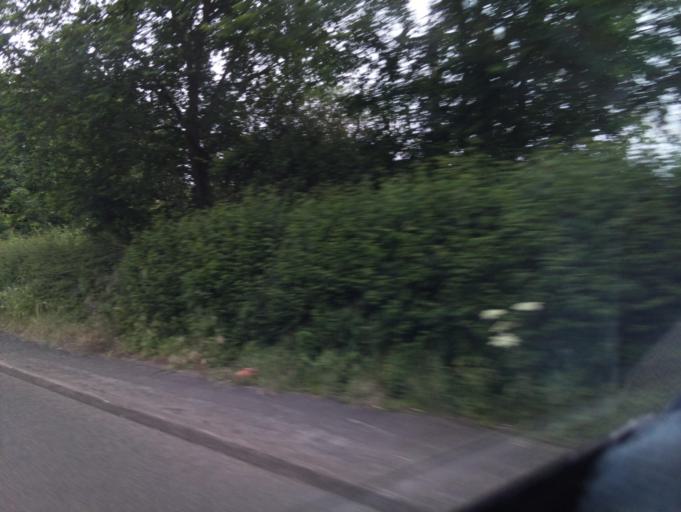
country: GB
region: England
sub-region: Derbyshire
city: Netherseal
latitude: 52.7276
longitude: -1.5606
